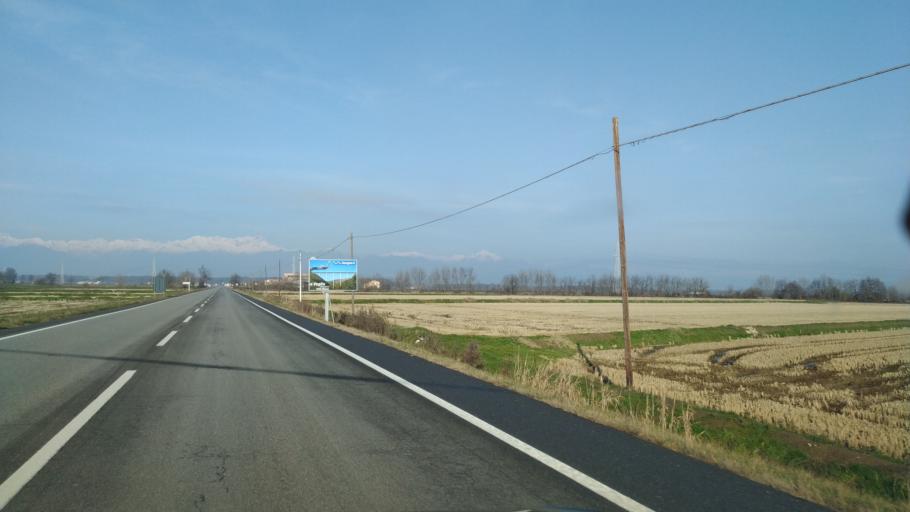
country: IT
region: Piedmont
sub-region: Provincia di Biella
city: Gifflenga
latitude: 45.4518
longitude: 8.2277
